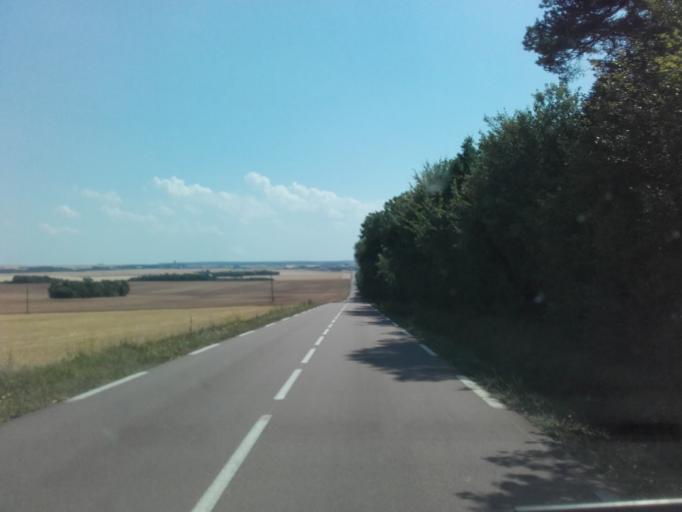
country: FR
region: Bourgogne
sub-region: Departement de l'Yonne
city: Joux-la-Ville
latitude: 47.7038
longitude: 3.8577
